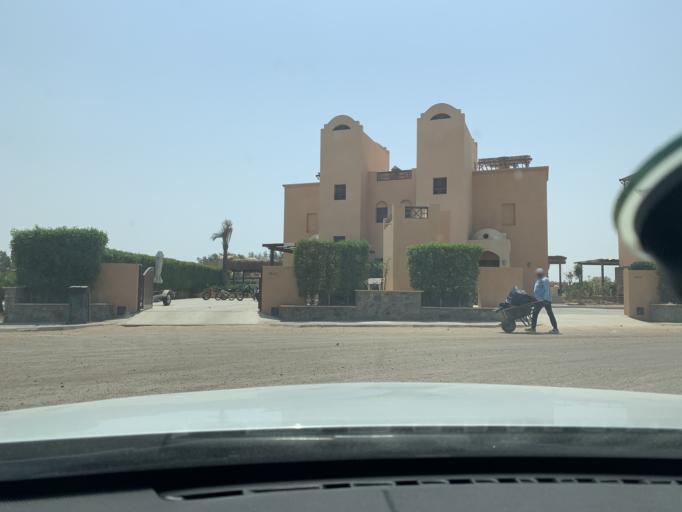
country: EG
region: Red Sea
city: El Gouna
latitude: 27.3877
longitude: 33.6691
